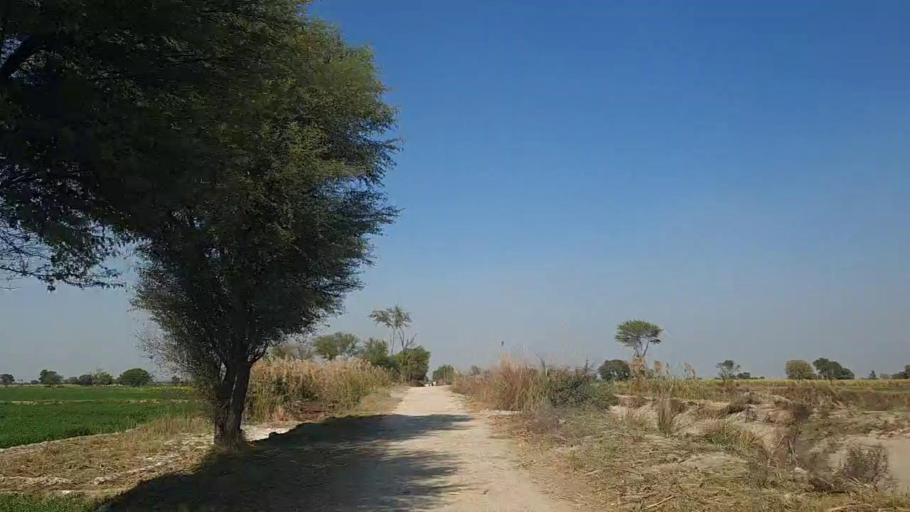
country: PK
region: Sindh
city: Sakrand
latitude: 26.2655
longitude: 68.2210
